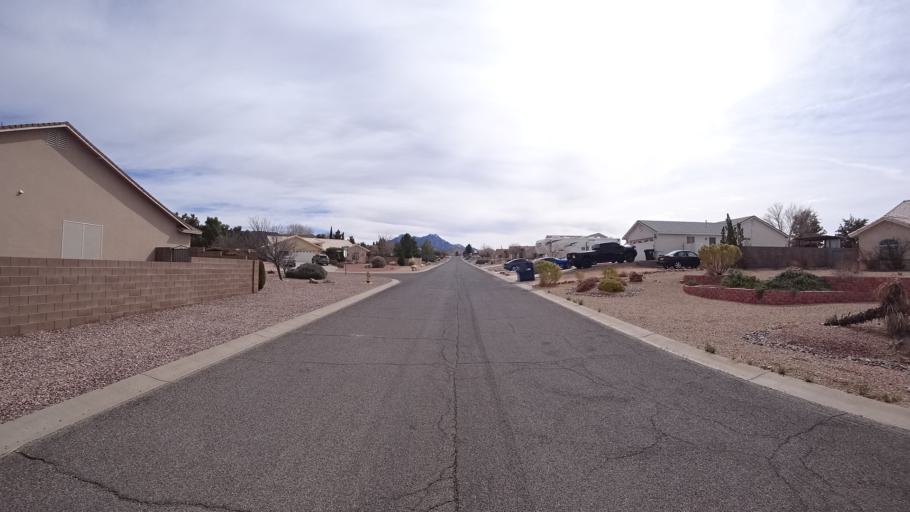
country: US
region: Arizona
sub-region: Mohave County
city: Kingman
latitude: 35.1940
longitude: -113.9816
